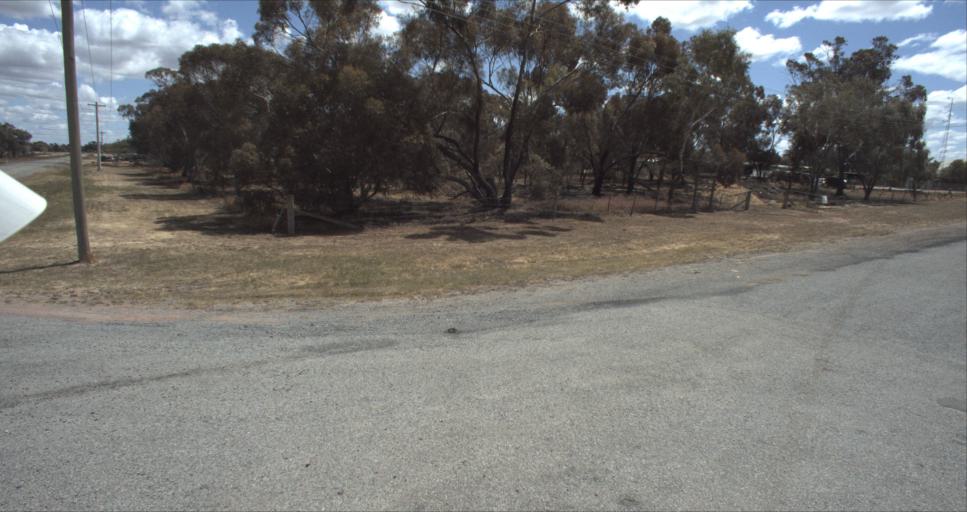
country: AU
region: New South Wales
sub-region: Murrumbidgee Shire
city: Darlington Point
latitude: -34.5195
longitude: 146.1802
